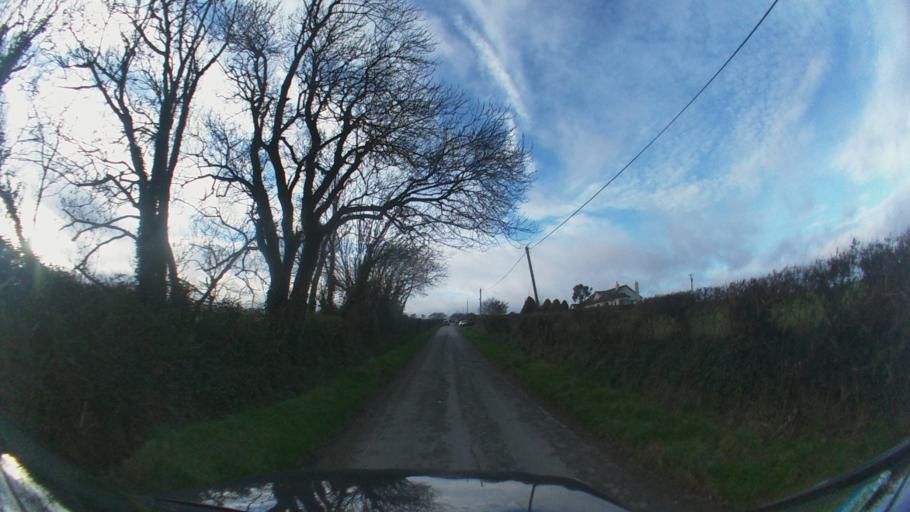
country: IE
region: Leinster
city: Balrothery
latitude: 53.5743
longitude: -6.1500
